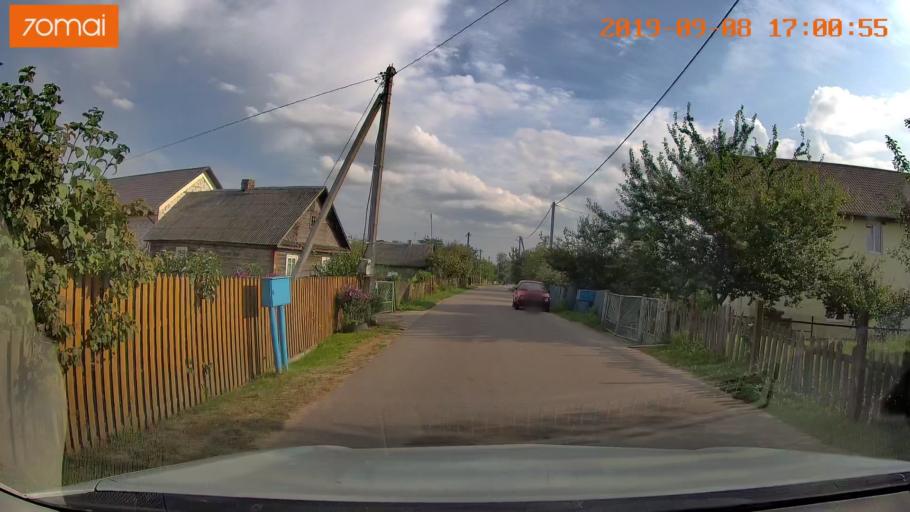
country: BY
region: Grodnenskaya
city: Hrodna
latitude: 53.7133
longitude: 23.9330
